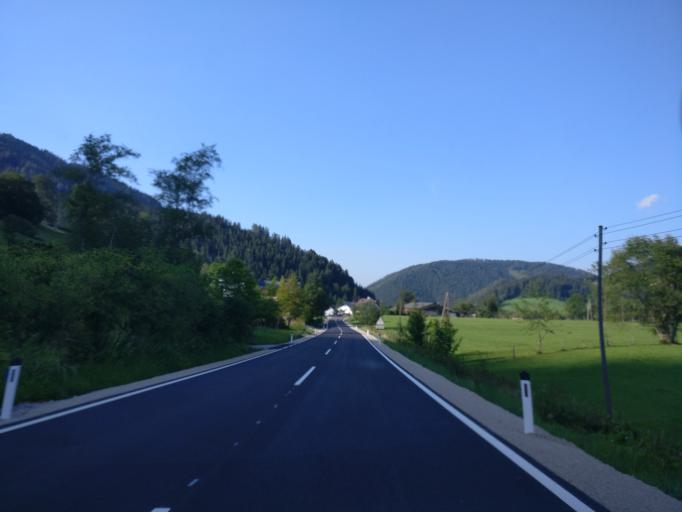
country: AT
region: Lower Austria
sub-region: Politischer Bezirk Scheibbs
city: Gostling an der Ybbs
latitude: 47.7508
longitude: 14.8995
